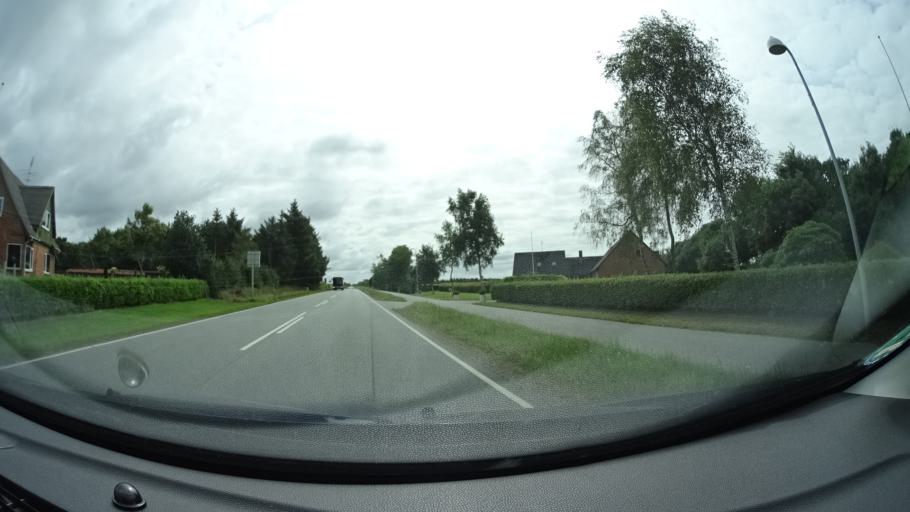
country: DK
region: South Denmark
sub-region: Tonder Kommune
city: Sherrebek
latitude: 55.1906
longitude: 8.7297
